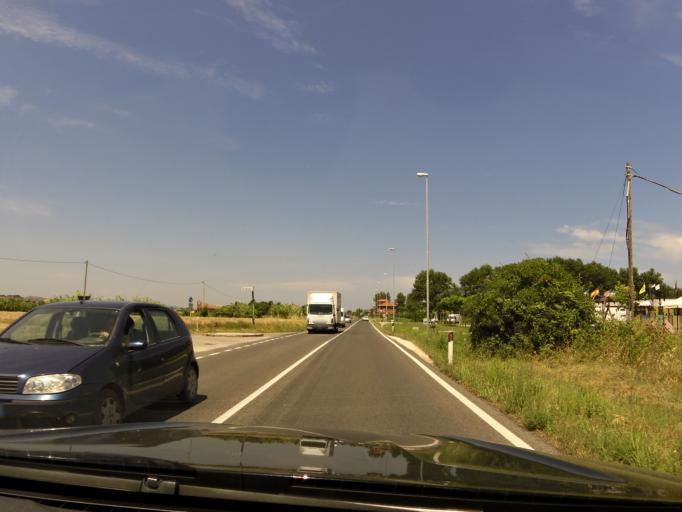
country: IT
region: The Marches
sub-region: Provincia di Pesaro e Urbino
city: Marotta
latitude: 43.7958
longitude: 13.0966
